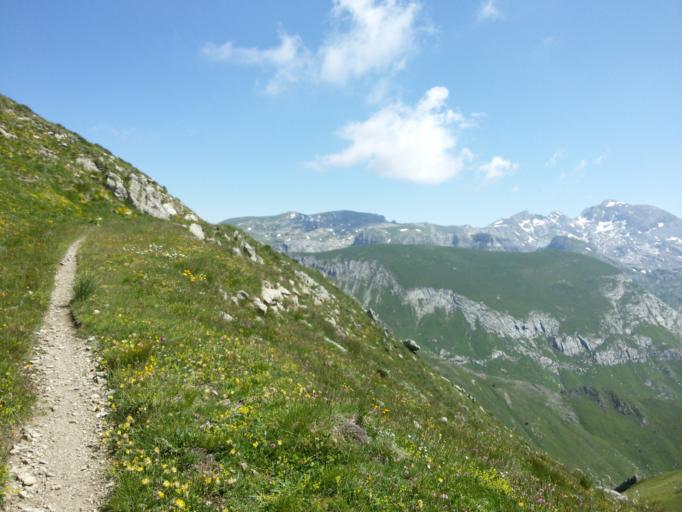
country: IT
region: Piedmont
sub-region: Provincia di Cuneo
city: Limone Piemonte
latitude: 44.1487
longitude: 7.6225
